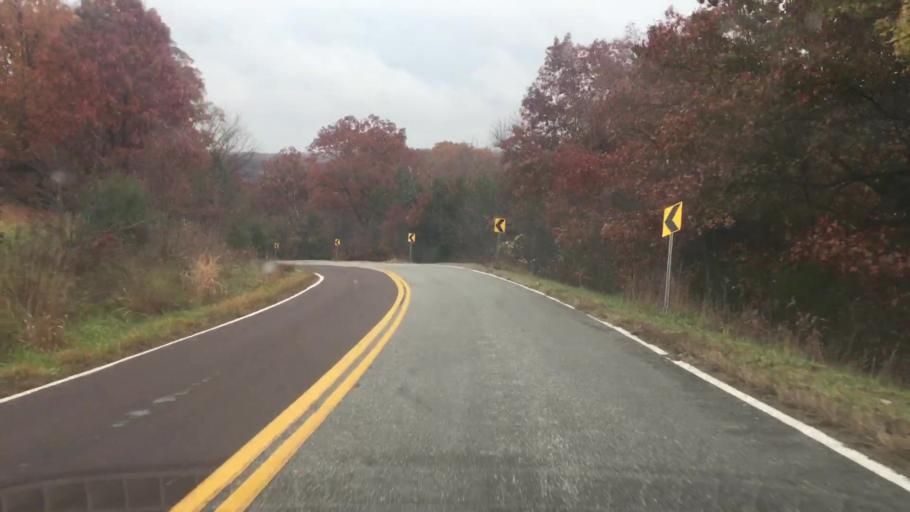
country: US
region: Missouri
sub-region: Callaway County
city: Fulton
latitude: 38.7936
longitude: -91.8816
